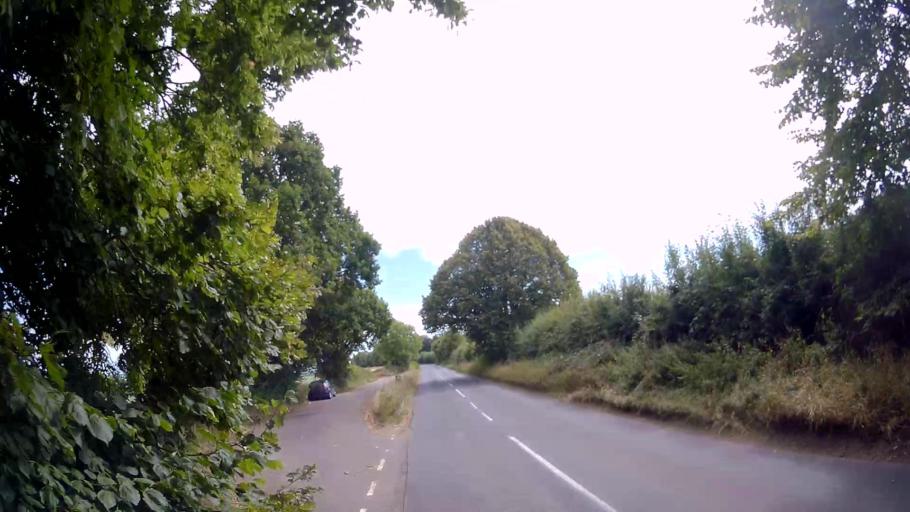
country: GB
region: England
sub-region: Hampshire
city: Long Sutton
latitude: 51.2253
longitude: -0.9536
